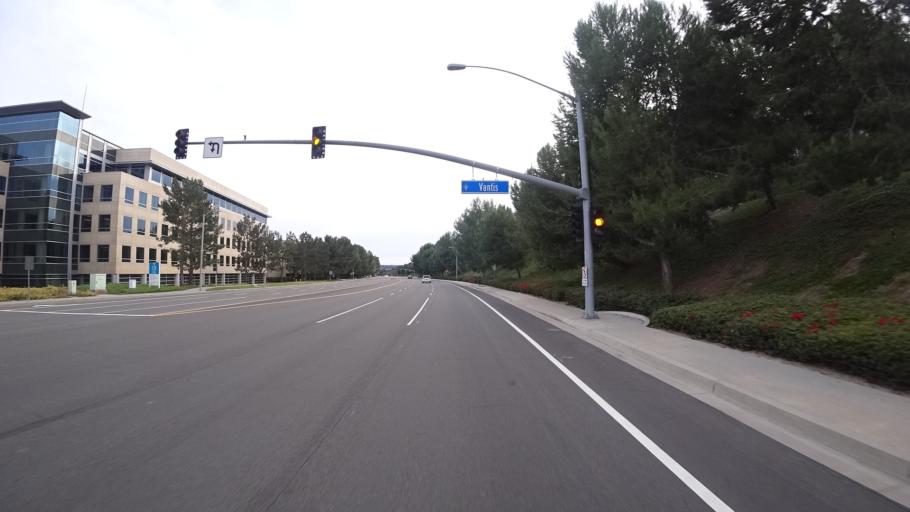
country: US
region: California
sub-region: Orange County
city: Aliso Viejo
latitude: 33.5796
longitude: -117.7306
